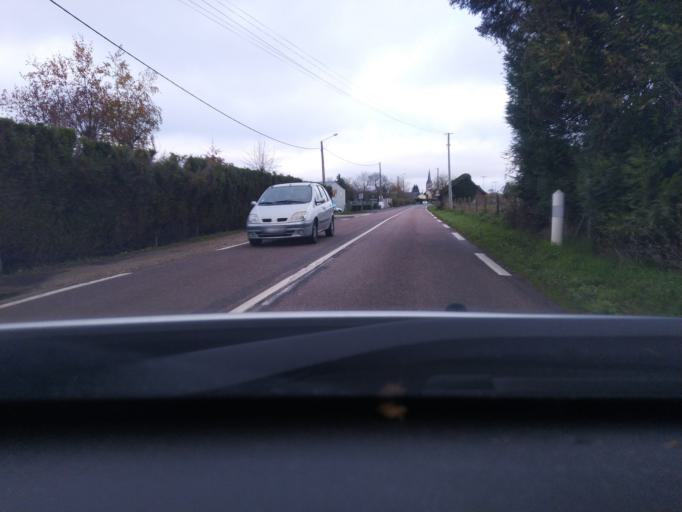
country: FR
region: Haute-Normandie
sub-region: Departement de la Seine-Maritime
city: Saint-Pierre-de-Varengeville
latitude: 49.4984
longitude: 0.9260
